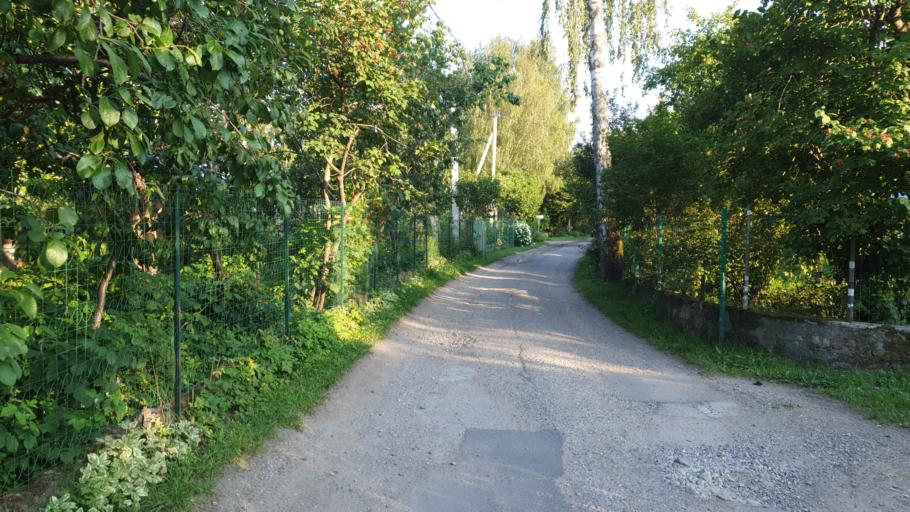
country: LT
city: Grigiskes
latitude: 54.7638
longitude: 25.0299
